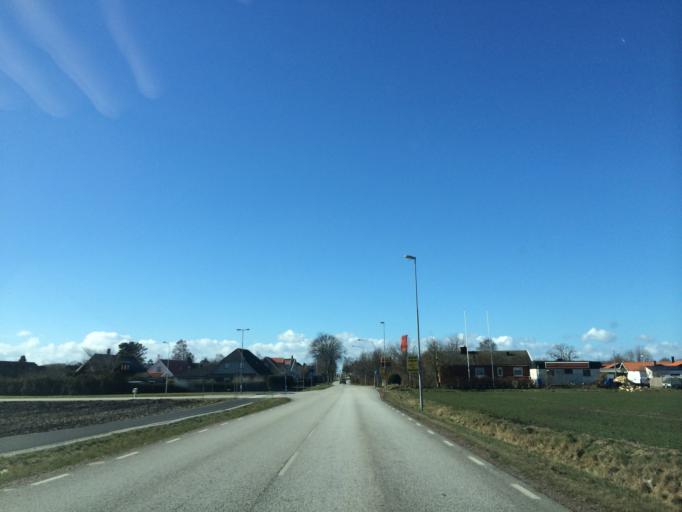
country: SE
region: Skane
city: Bjarred
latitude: 55.7201
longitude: 13.0394
